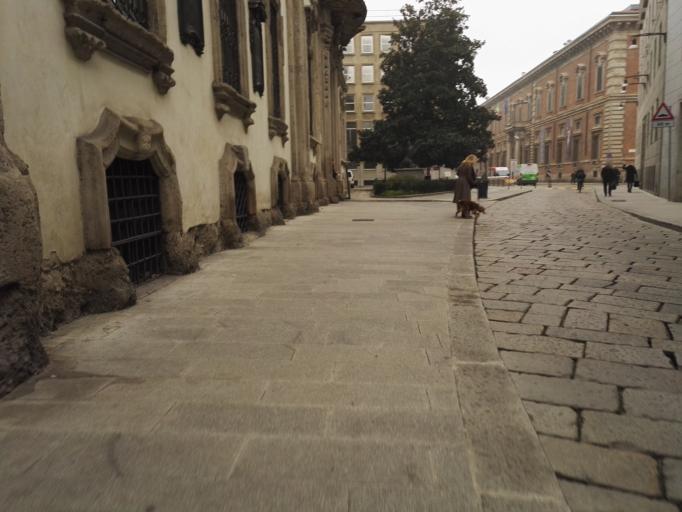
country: IT
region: Lombardy
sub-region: Citta metropolitana di Milano
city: Milano
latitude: 45.4709
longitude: 9.1876
